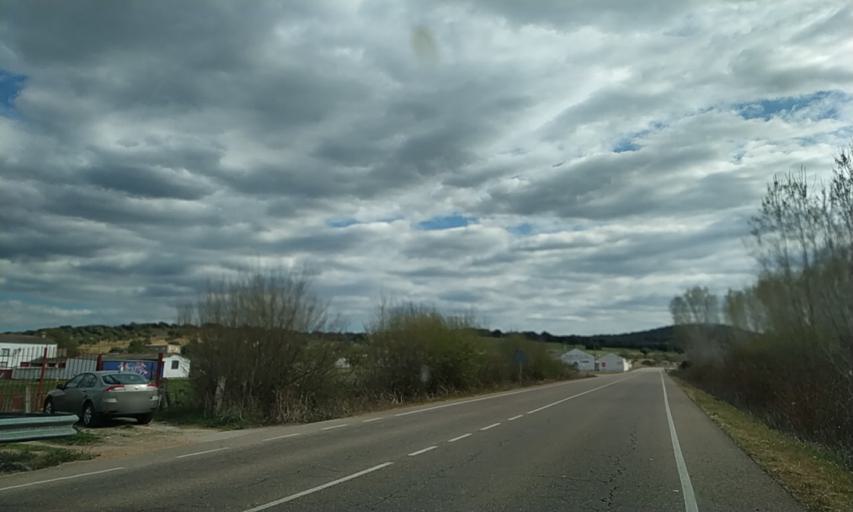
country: ES
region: Castille and Leon
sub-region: Provincia de Salamanca
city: Ciudad Rodrigo
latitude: 40.5820
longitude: -6.5376
